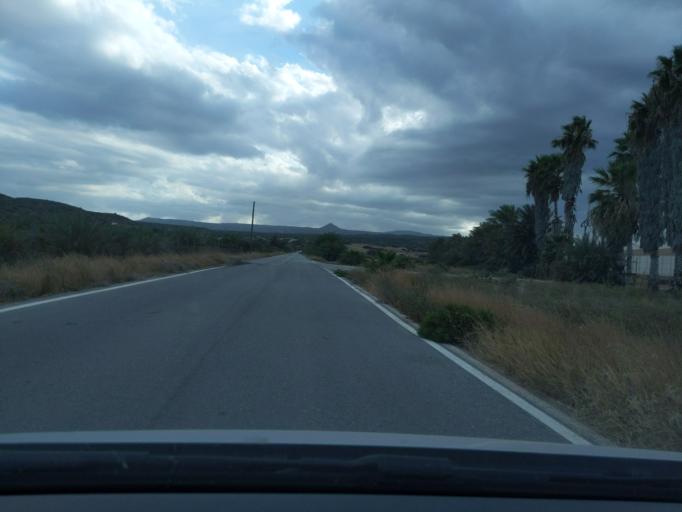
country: GR
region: Crete
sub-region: Nomos Lasithiou
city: Palekastro
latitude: 35.2600
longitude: 26.2564
